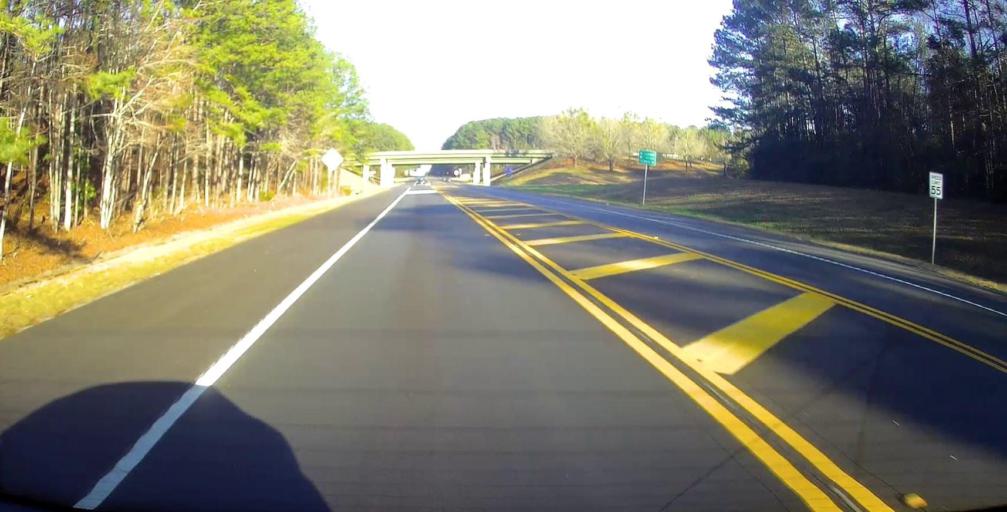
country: US
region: Georgia
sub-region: Harris County
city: Hamilton
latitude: 32.7472
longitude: -85.0201
